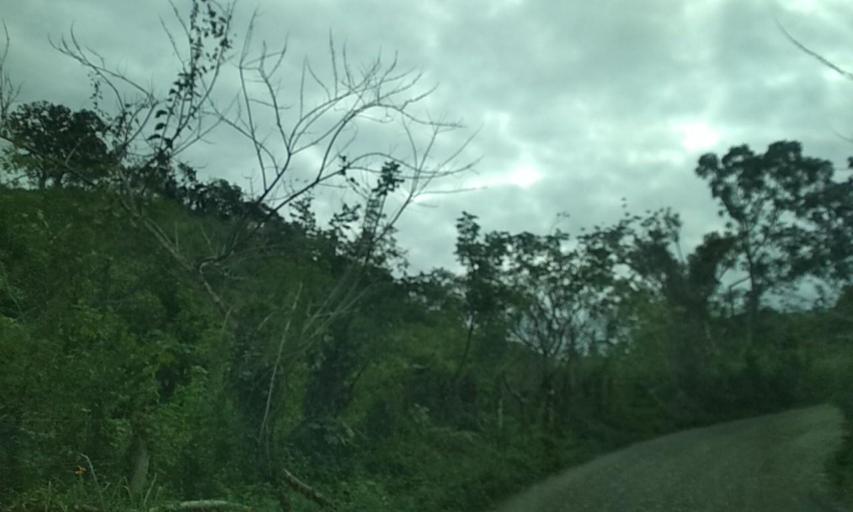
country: MX
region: Veracruz
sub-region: Papantla
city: Residencial Tajin
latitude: 20.6209
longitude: -97.3618
